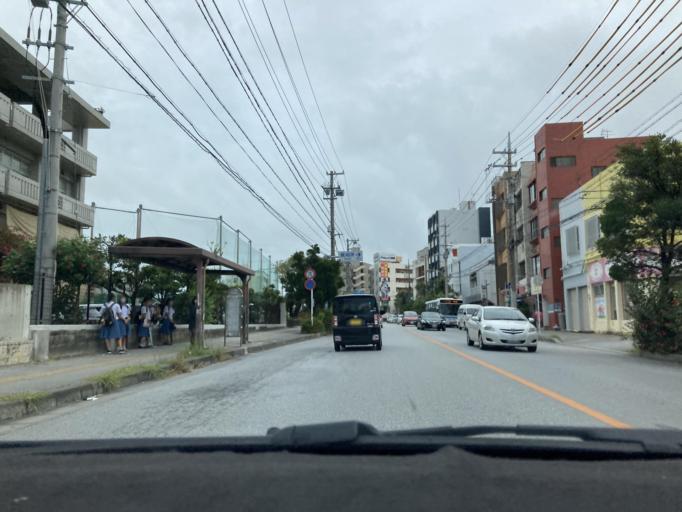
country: JP
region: Okinawa
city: Naha-shi
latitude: 26.2108
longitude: 127.6841
